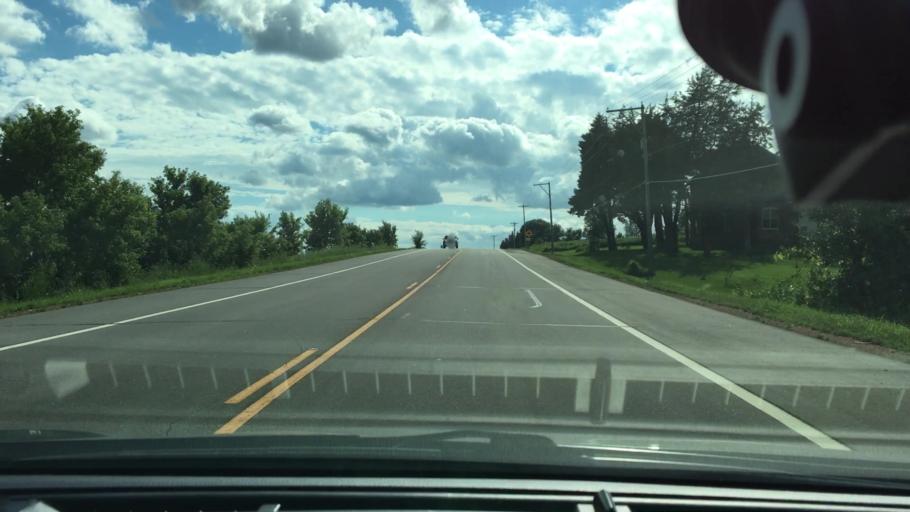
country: US
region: Minnesota
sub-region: Hennepin County
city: Saint Bonifacius
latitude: 44.9190
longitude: -93.7337
